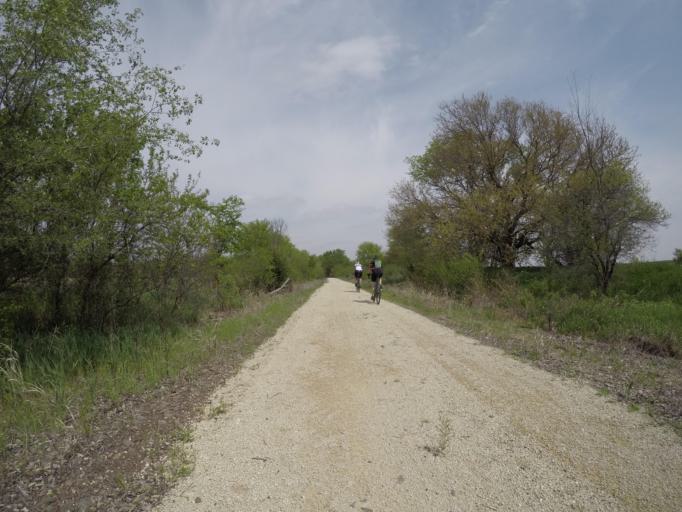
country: US
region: Nebraska
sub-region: Gage County
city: Wymore
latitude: 40.1824
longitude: -96.6595
